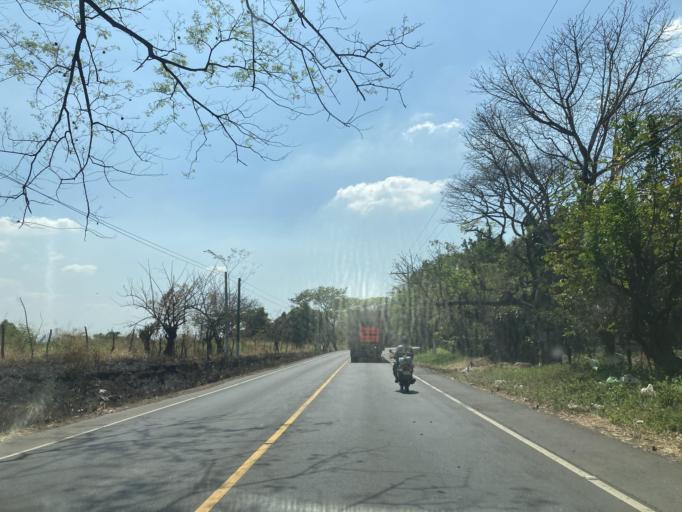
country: GT
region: Escuintla
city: Guanagazapa
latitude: 14.2152
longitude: -90.7242
